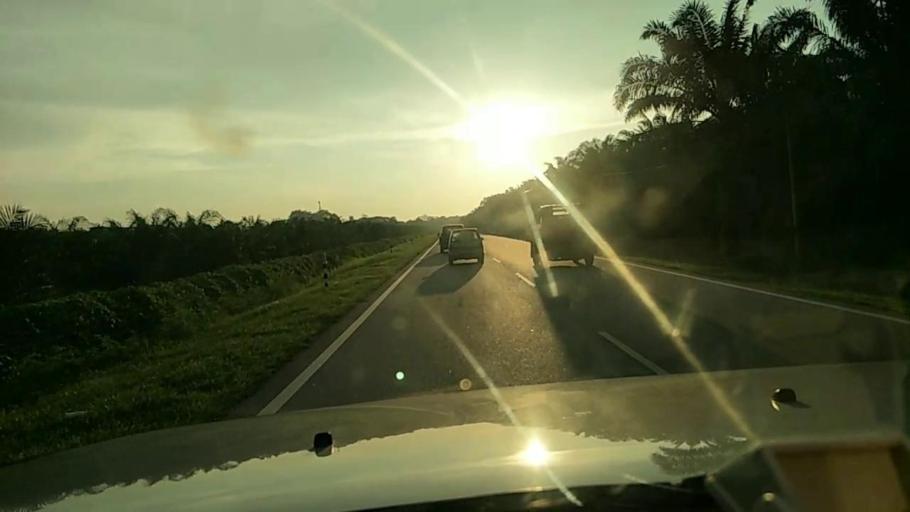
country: MY
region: Selangor
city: Kuala Selangor
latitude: 3.3088
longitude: 101.3266
